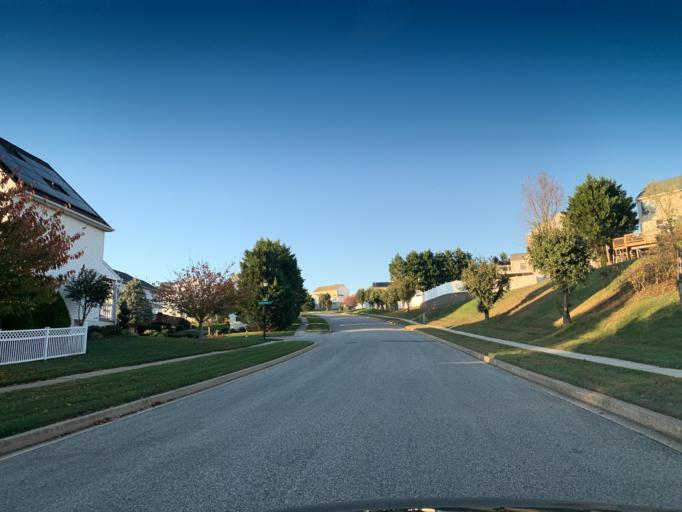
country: US
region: Maryland
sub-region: Harford County
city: Bel Air North
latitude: 39.5643
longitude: -76.3830
